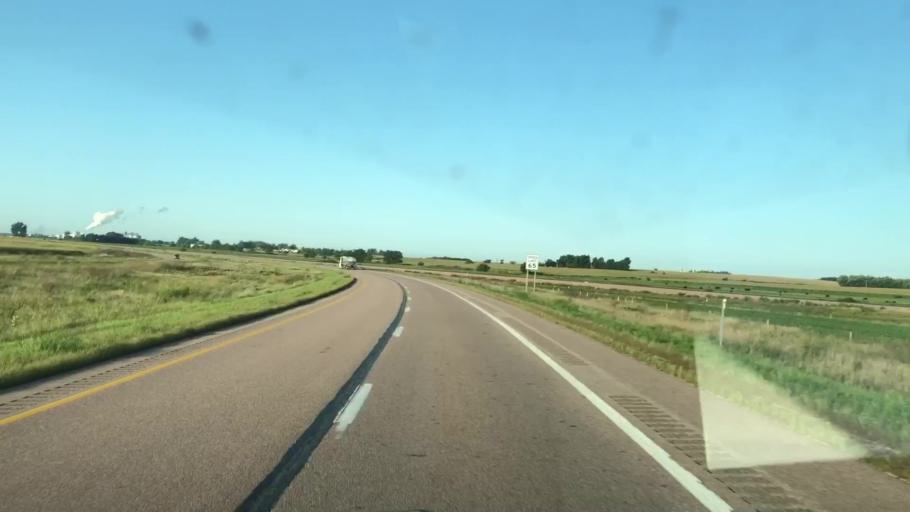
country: US
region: Iowa
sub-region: Osceola County
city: Sibley
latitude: 43.3008
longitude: -95.7905
